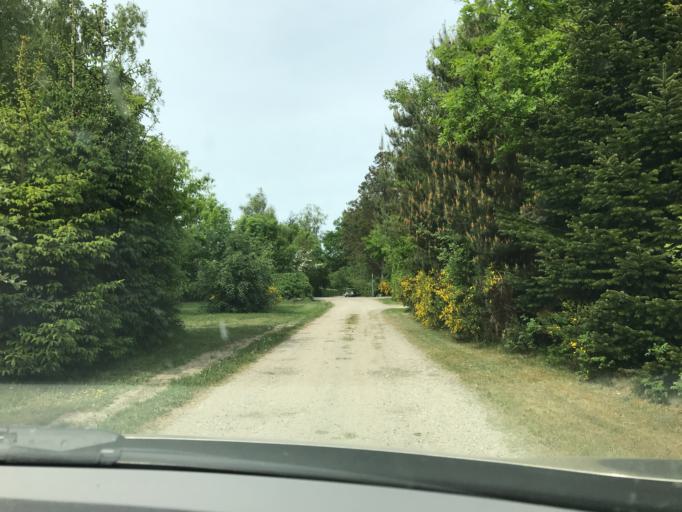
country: DK
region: Central Jutland
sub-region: Norddjurs Kommune
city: Allingabro
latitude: 56.5926
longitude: 10.3154
